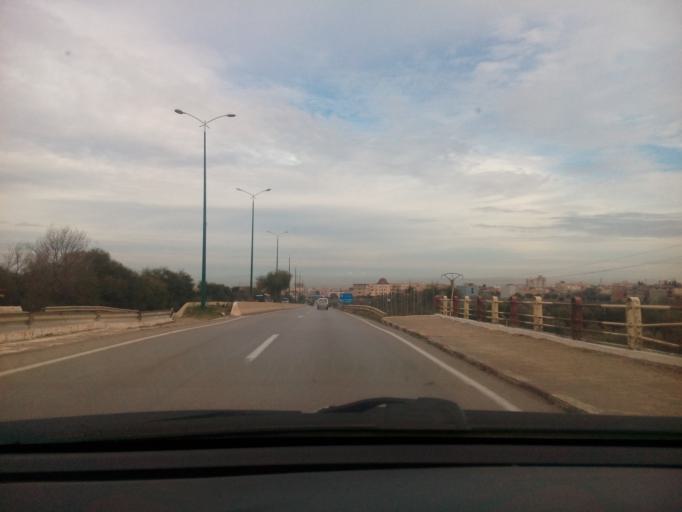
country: DZ
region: Tlemcen
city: Mansoura
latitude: 34.8711
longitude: -1.3497
